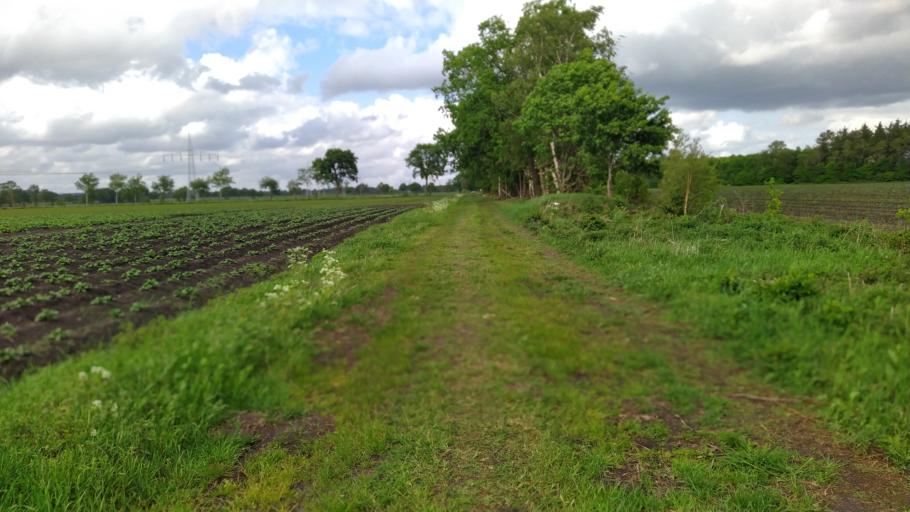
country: DE
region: Lower Saxony
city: Brest
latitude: 53.4556
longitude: 9.4043
